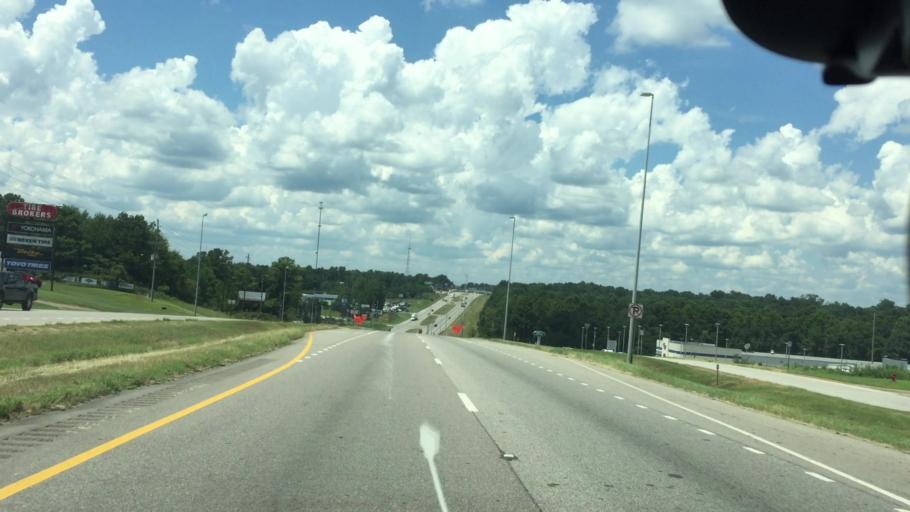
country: US
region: Alabama
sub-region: Pike County
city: Troy
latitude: 31.7944
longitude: -85.9793
